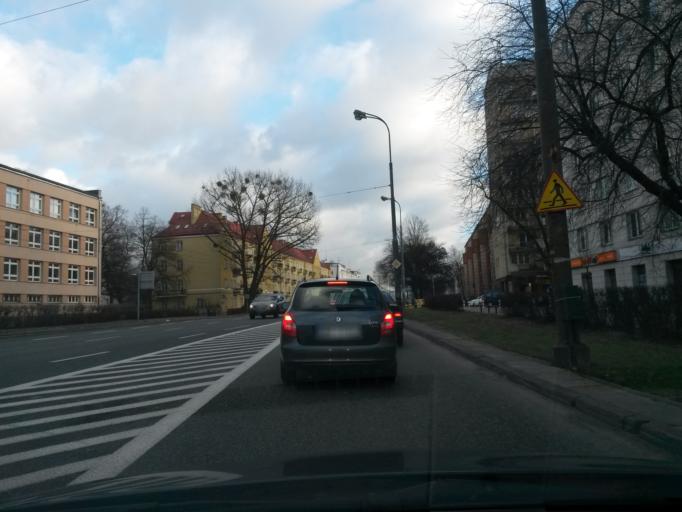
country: PL
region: Masovian Voivodeship
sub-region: Warszawa
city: Zoliborz
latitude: 52.2712
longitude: 20.9751
